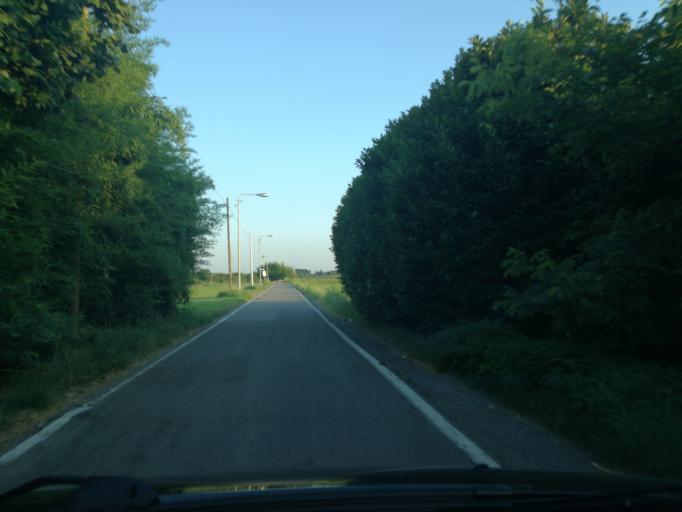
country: IT
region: Lombardy
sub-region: Provincia di Monza e Brianza
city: Porto d'Adda
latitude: 45.6636
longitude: 9.4680
